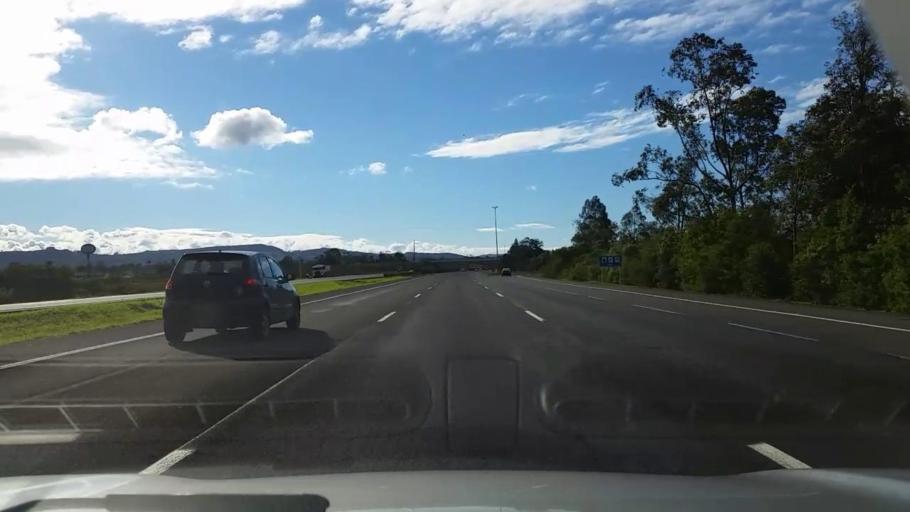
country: BR
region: Rio Grande do Sul
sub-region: Rolante
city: Rolante
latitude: -29.8806
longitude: -50.5160
